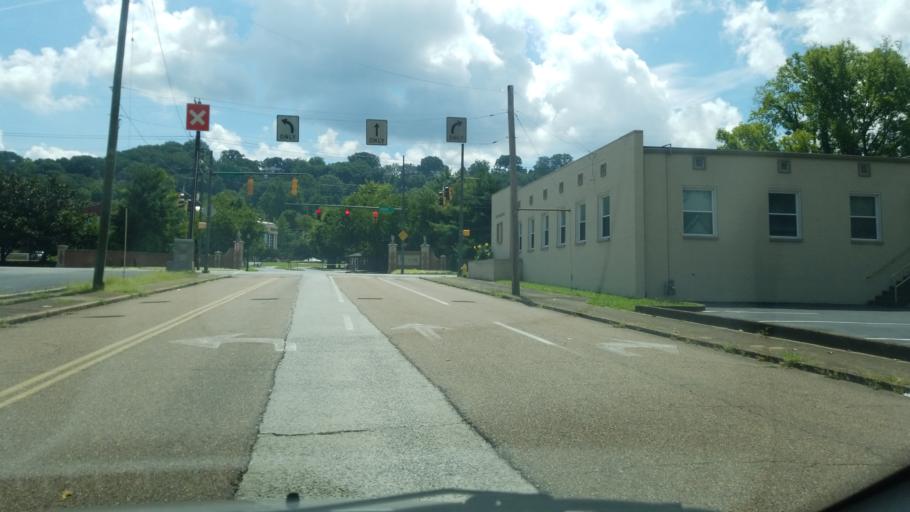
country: US
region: Tennessee
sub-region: Hamilton County
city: East Ridge
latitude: 35.0296
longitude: -85.2659
